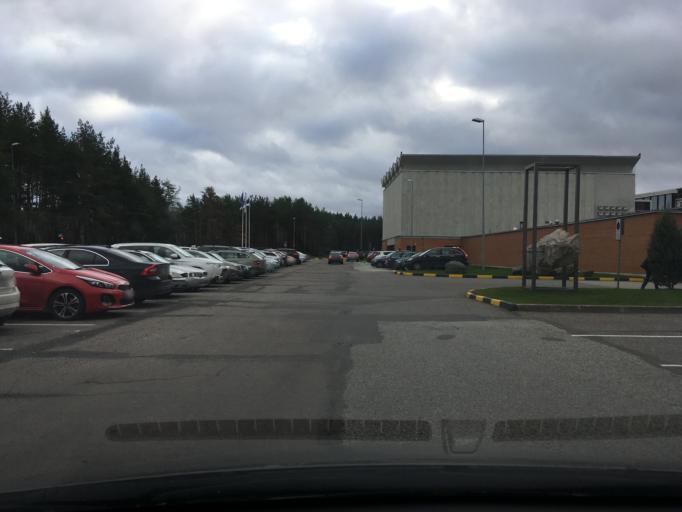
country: EE
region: Harju
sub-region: Saue vald
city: Laagri
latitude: 59.3962
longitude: 24.6720
